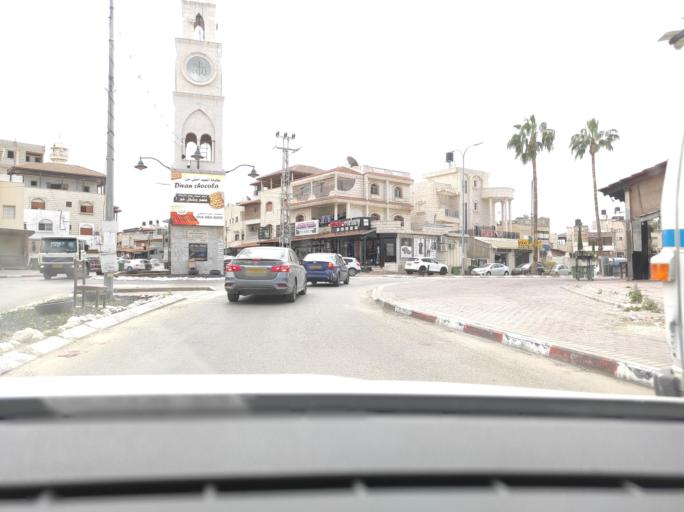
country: IL
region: Central District
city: Kafr Qasim
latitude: 32.1177
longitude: 34.9687
